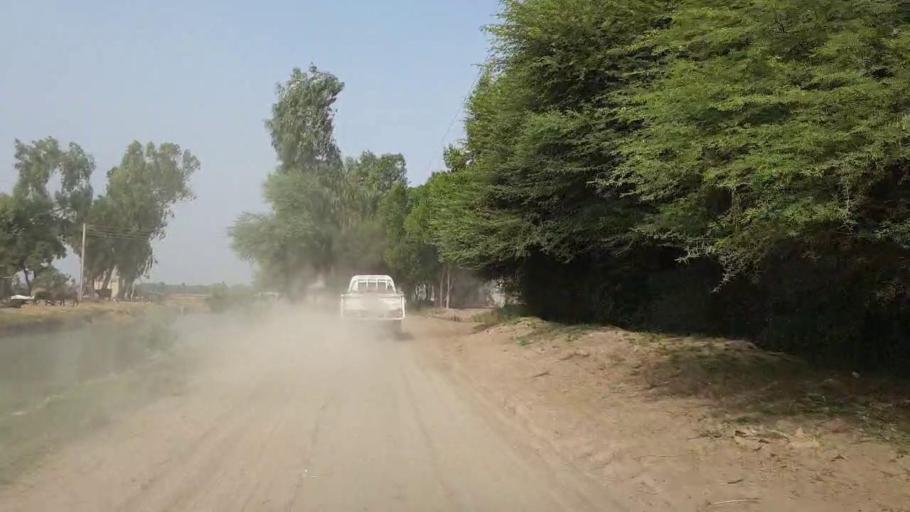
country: PK
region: Sindh
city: Kario
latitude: 24.8346
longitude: 68.5438
